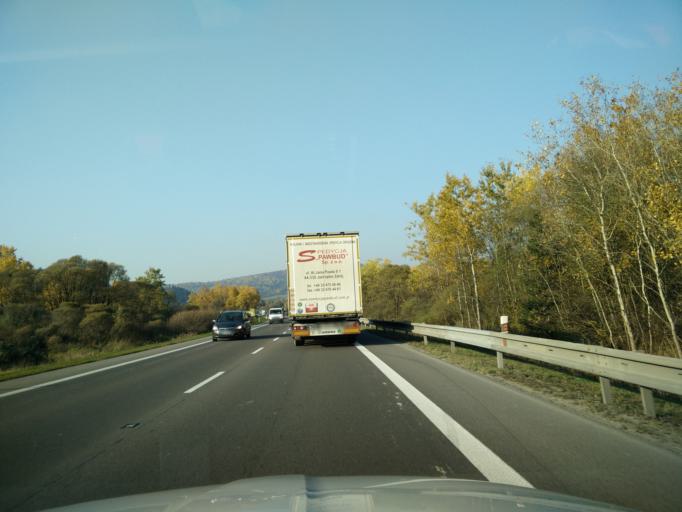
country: SK
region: Zilinsky
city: Cadca
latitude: 49.4090
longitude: 18.8426
